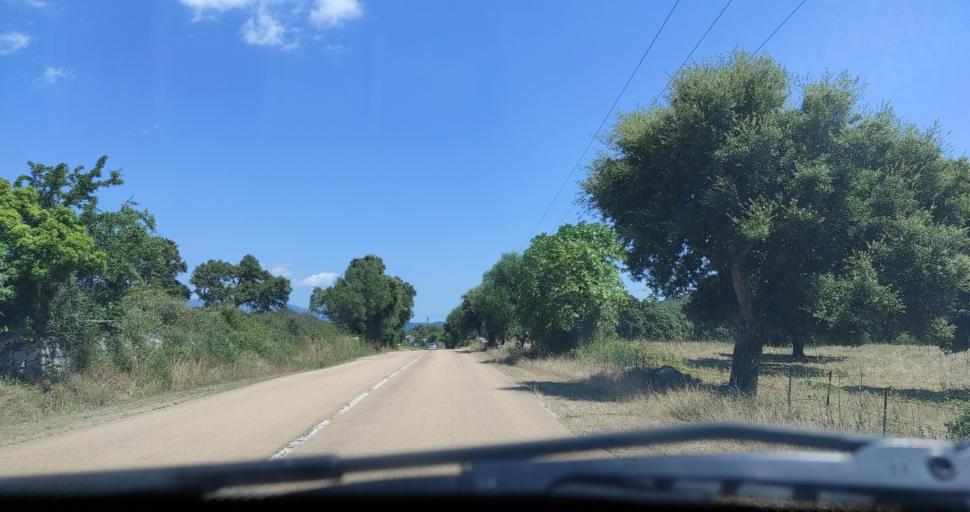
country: FR
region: Corsica
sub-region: Departement de la Corse-du-Sud
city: Porto-Vecchio
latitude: 41.5402
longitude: 9.1768
